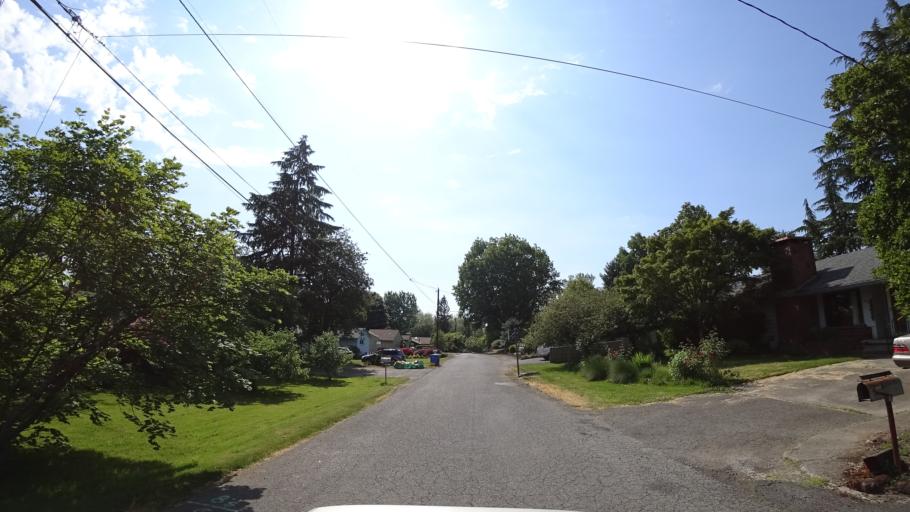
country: US
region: Oregon
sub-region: Washington County
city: Metzger
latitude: 45.4534
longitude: -122.7417
